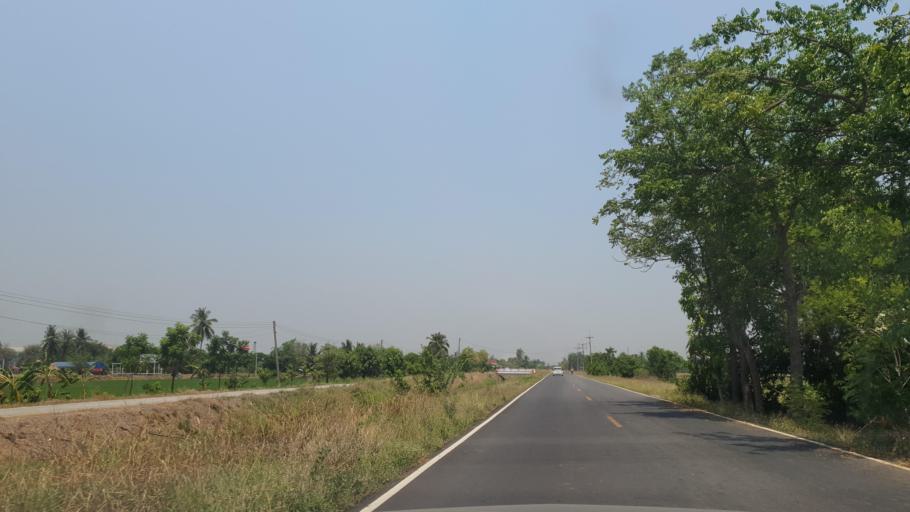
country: TH
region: Suphan Buri
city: Si Prachan
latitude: 14.6236
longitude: 100.0944
